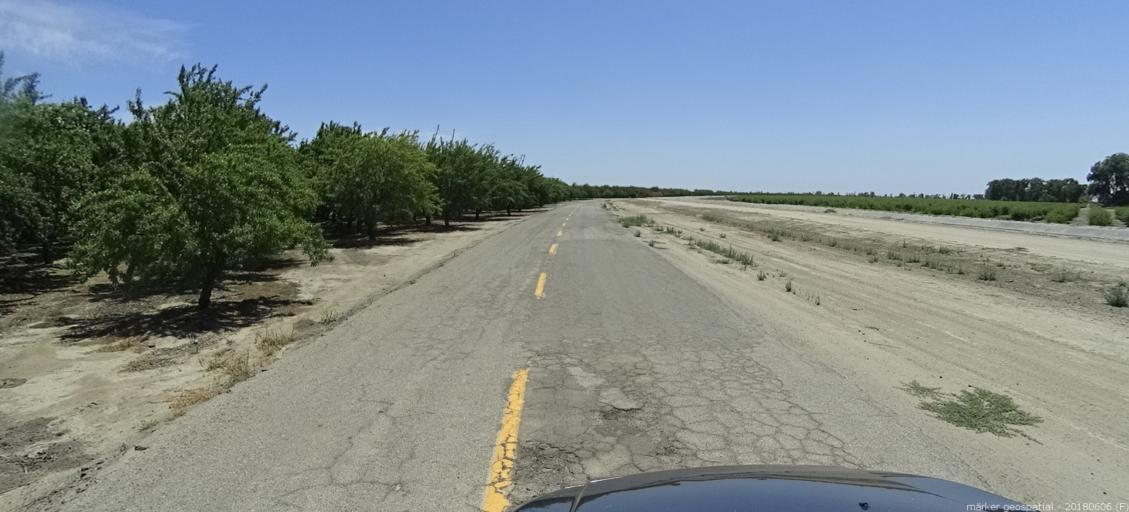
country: US
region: California
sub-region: Fresno County
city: Firebaugh
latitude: 36.8406
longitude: -120.4089
